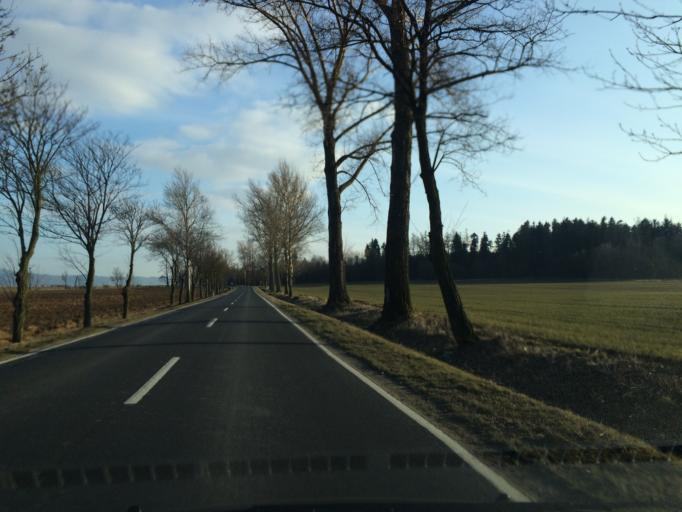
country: PL
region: Lower Silesian Voivodeship
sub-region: Powiat klodzki
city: Bystrzyca Klodzka
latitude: 50.2408
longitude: 16.6734
